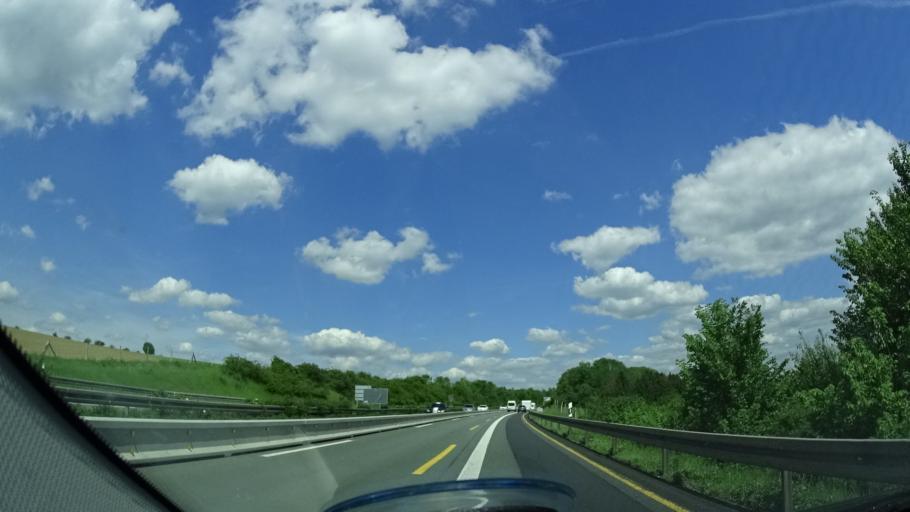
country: DE
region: North Rhine-Westphalia
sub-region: Regierungsbezirk Detmold
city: Paderborn
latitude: 51.6604
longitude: 8.7079
